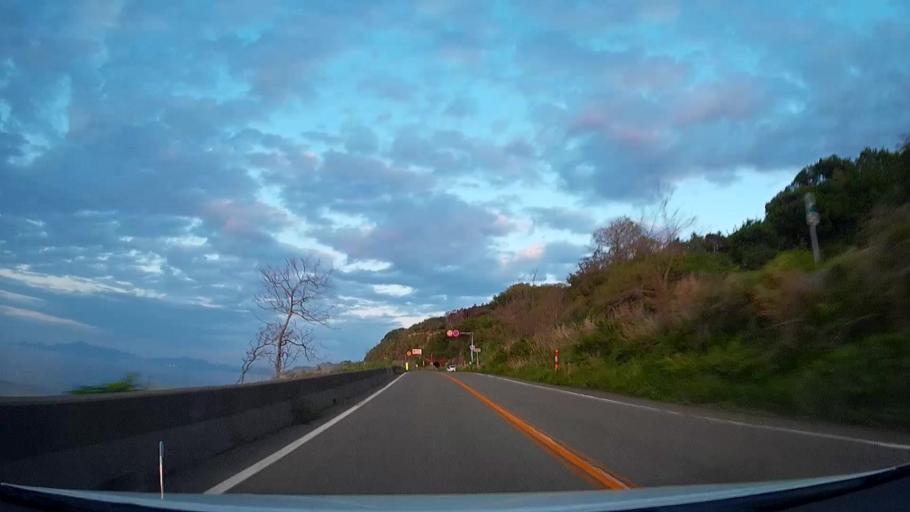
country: JP
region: Niigata
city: Joetsu
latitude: 37.1712
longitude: 138.1143
